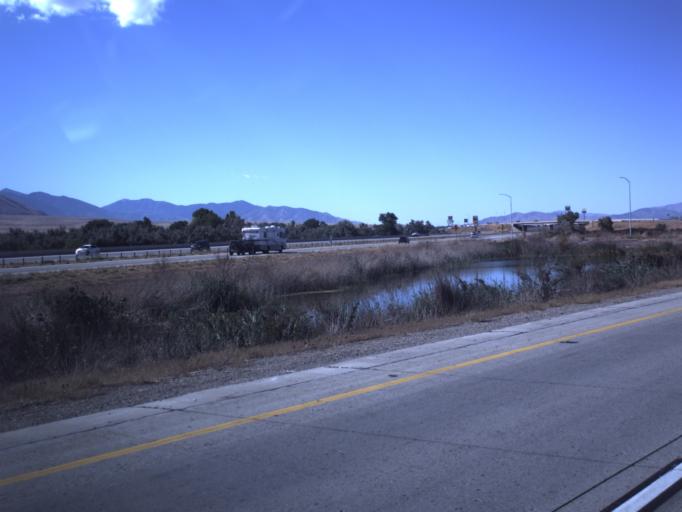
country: US
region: Utah
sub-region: Tooele County
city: Stansbury park
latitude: 40.6990
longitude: -112.2601
